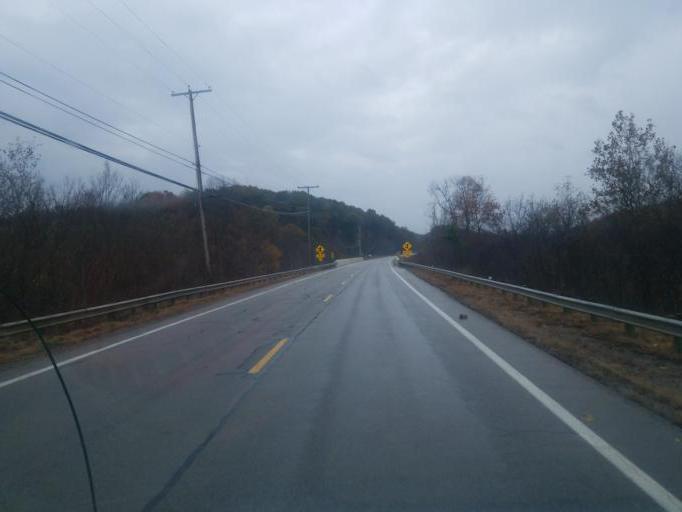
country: US
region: Ohio
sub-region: Muskingum County
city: Frazeysburg
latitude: 40.0236
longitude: -82.0942
